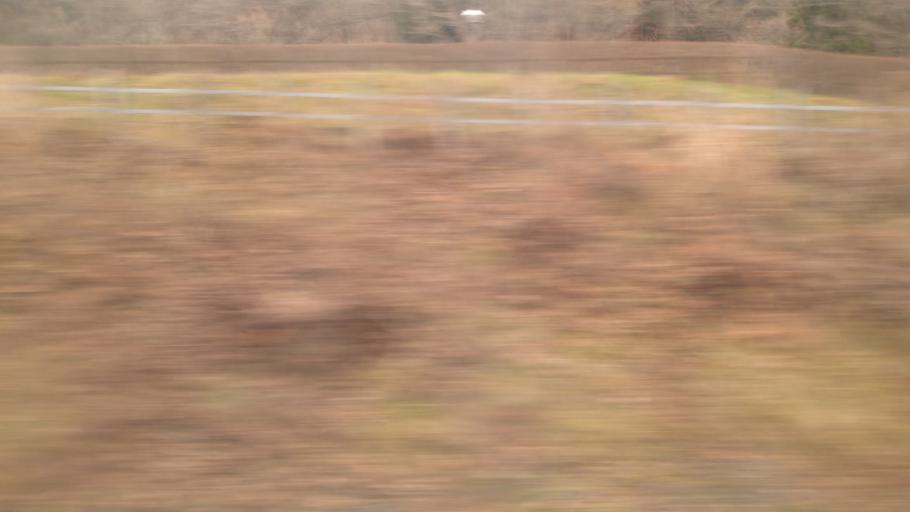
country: JP
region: Nagano
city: Shiojiri
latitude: 36.0513
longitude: 137.8962
